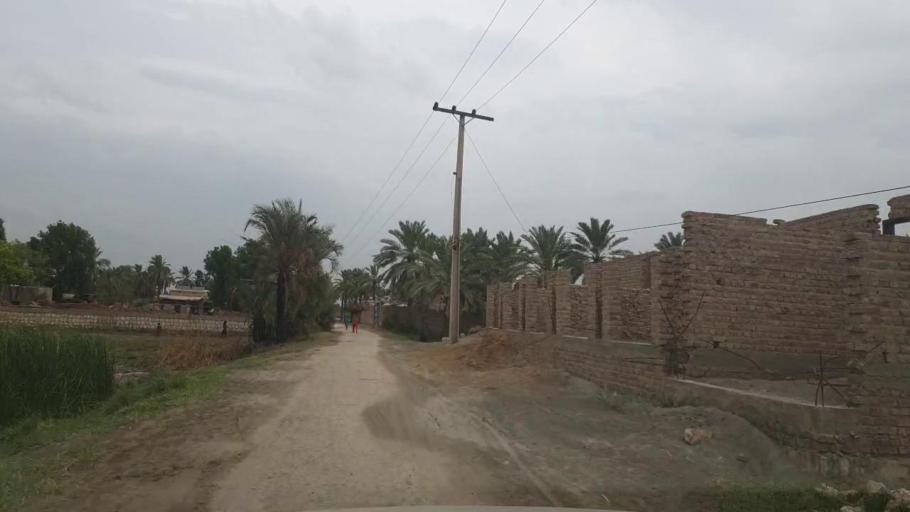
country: PK
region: Sindh
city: Khairpur
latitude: 27.5466
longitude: 68.7395
